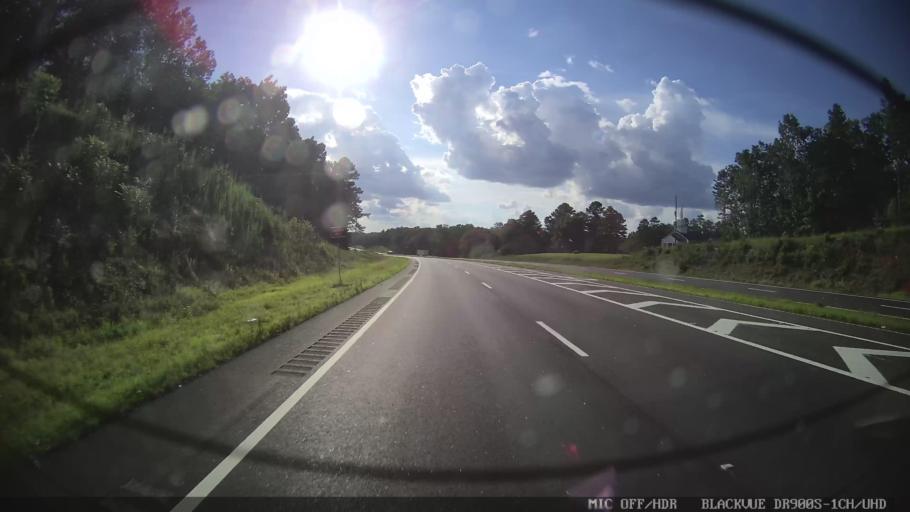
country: US
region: Georgia
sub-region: Floyd County
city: Rome
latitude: 34.2134
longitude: -85.1030
